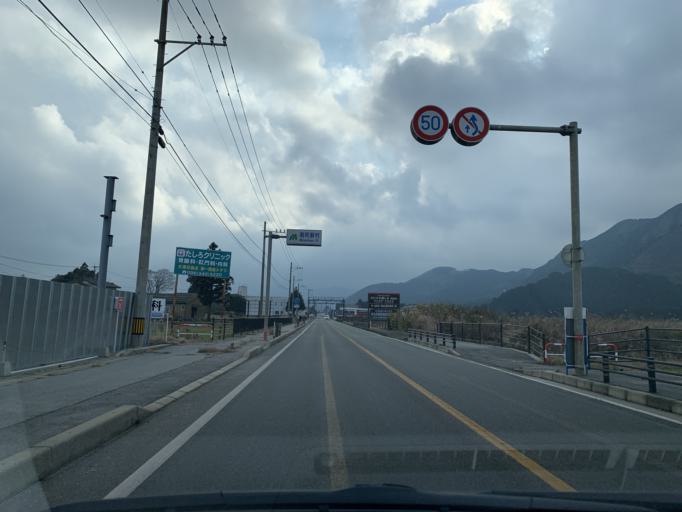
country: JP
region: Kumamoto
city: Aso
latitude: 32.9102
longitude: 130.9934
